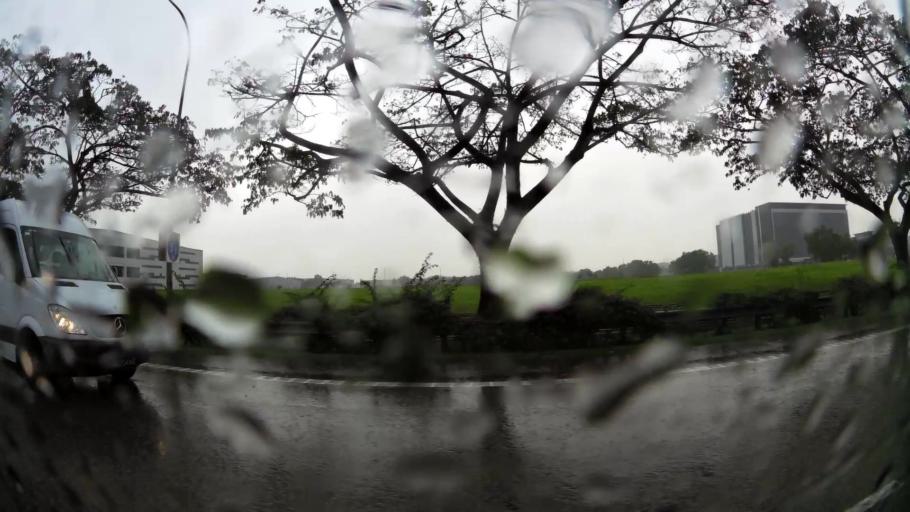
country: MY
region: Johor
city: Kampung Pasir Gudang Baru
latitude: 1.3774
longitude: 103.9277
